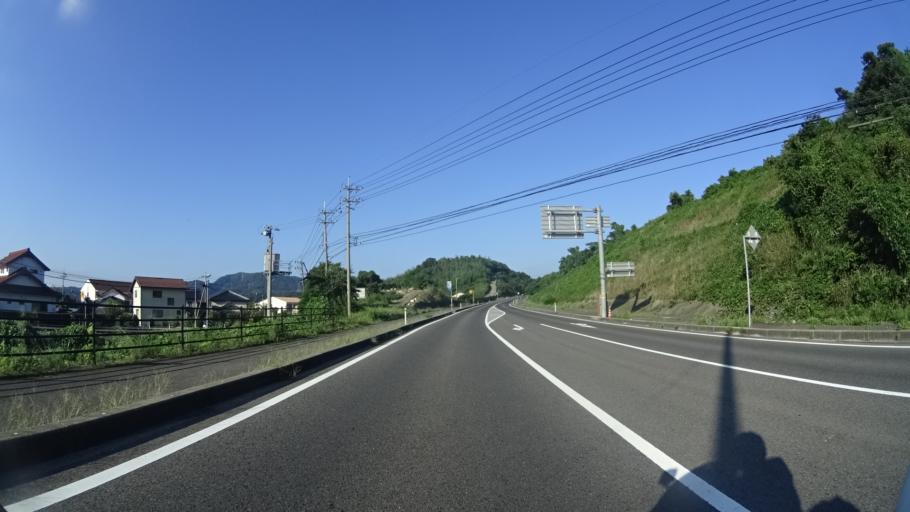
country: JP
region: Shimane
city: Matsue-shi
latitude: 35.5168
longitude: 133.1351
